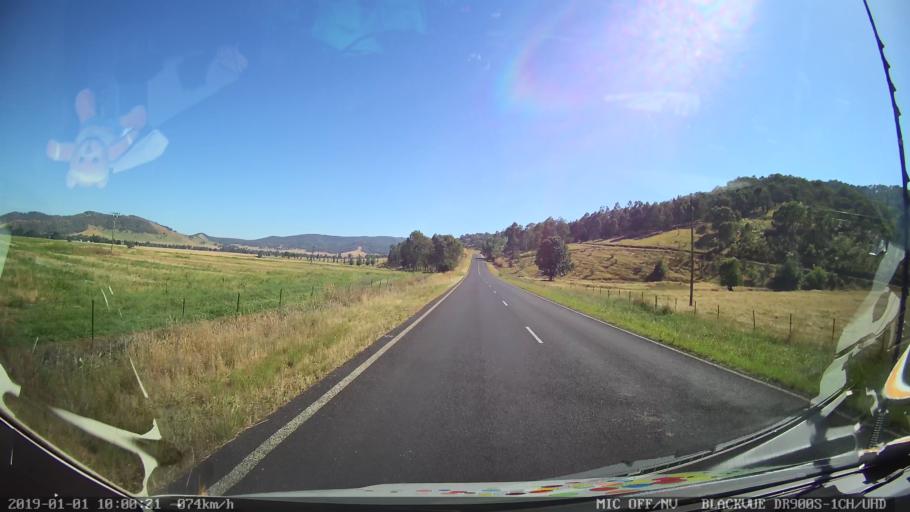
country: AU
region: New South Wales
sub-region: Snowy River
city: Jindabyne
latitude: -36.2033
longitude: 148.1017
